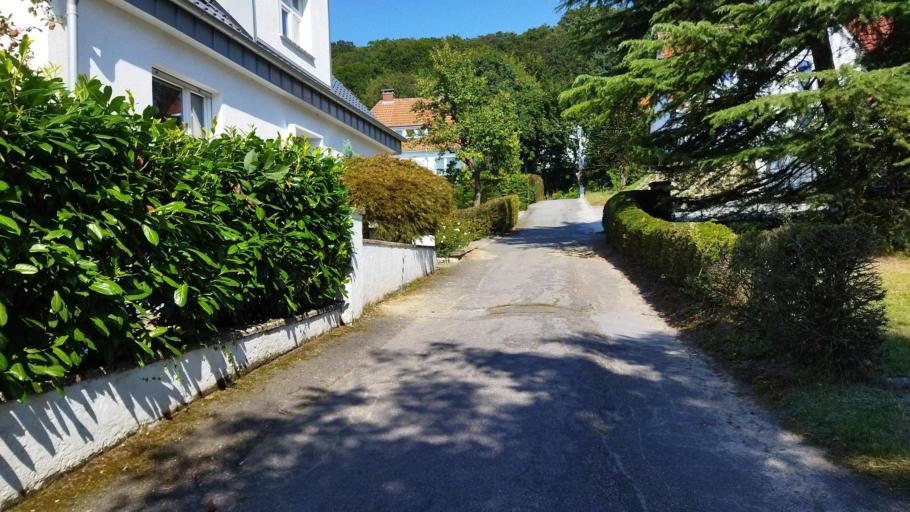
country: DE
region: North Rhine-Westphalia
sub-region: Regierungsbezirk Munster
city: Tecklenburg
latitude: 52.2159
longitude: 7.8072
